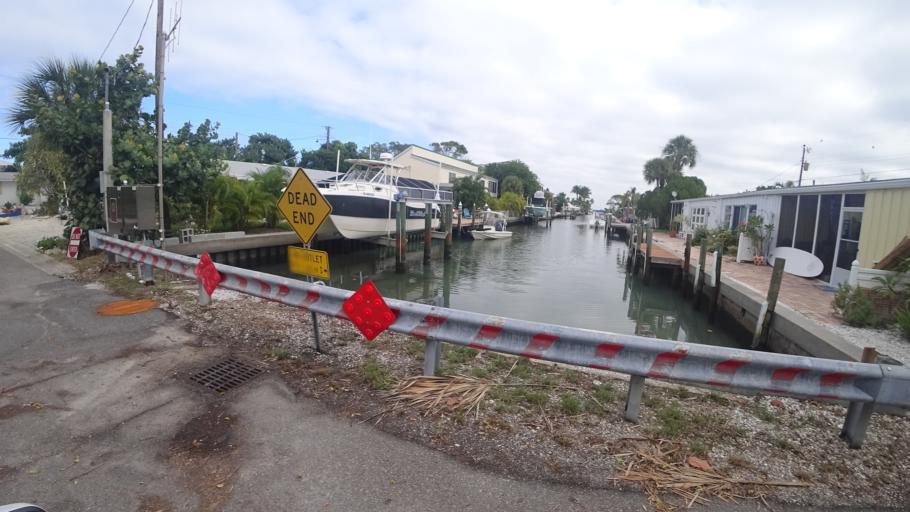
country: US
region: Florida
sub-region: Manatee County
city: Longboat Key
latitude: 27.4156
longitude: -82.6579
